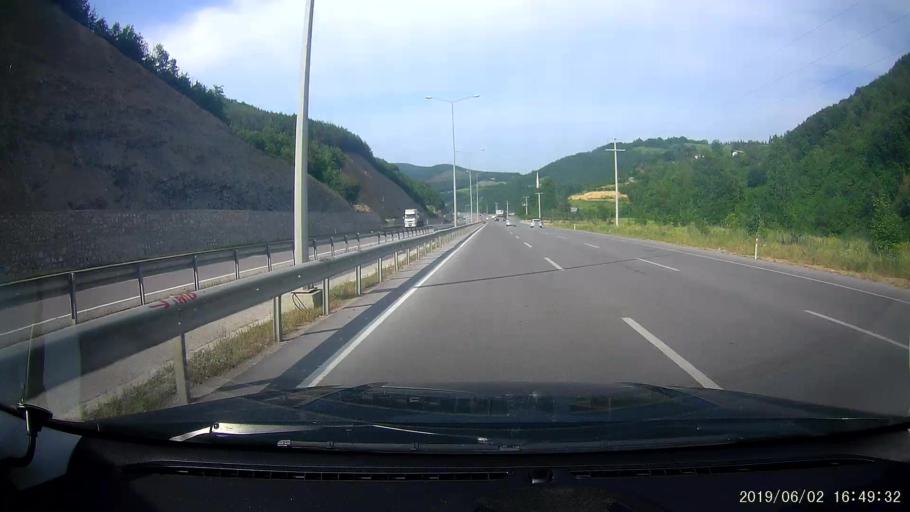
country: TR
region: Samsun
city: Samsun
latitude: 41.2391
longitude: 36.1641
